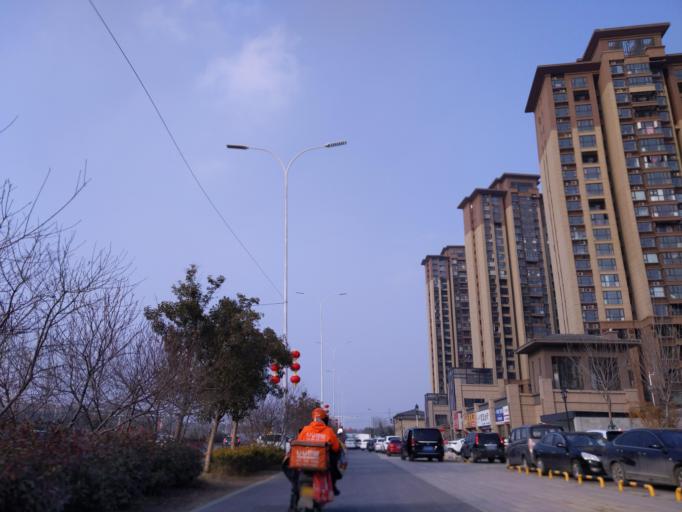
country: CN
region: Henan Sheng
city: Puyang
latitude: 35.8147
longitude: 115.0226
